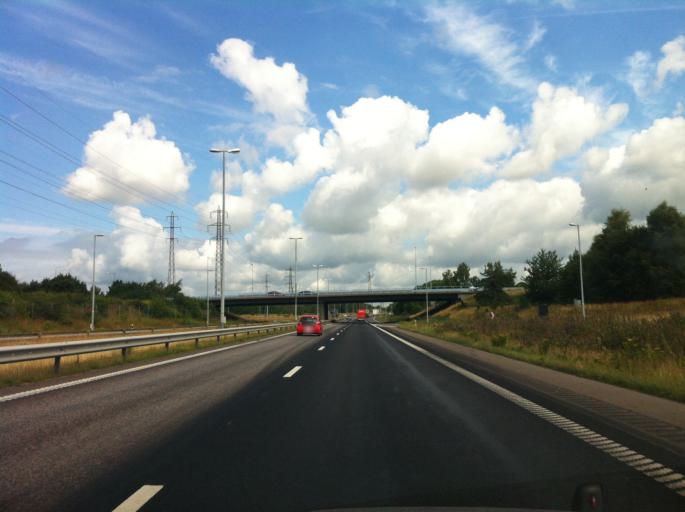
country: SE
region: Halland
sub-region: Halmstads Kommun
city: Fyllinge
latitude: 56.6727
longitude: 12.9000
